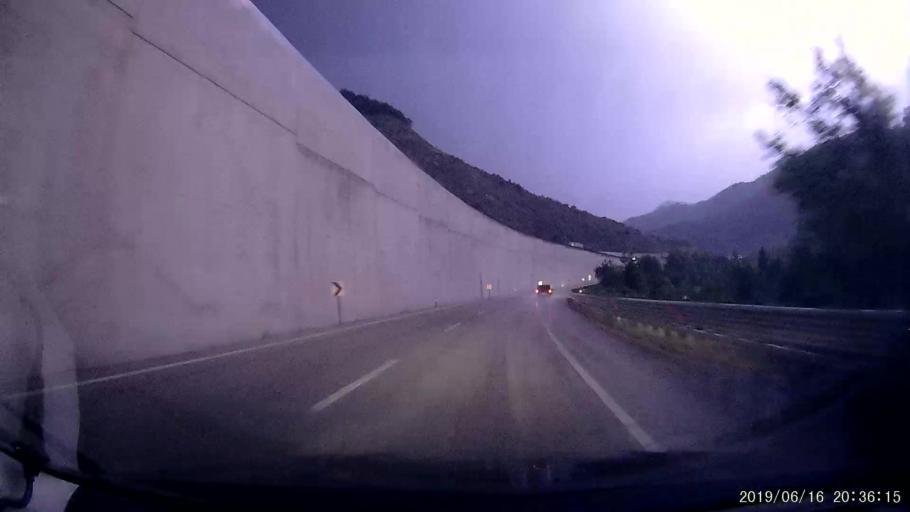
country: TR
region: Tokat
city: Basciftlik
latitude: 40.4449
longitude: 37.0787
